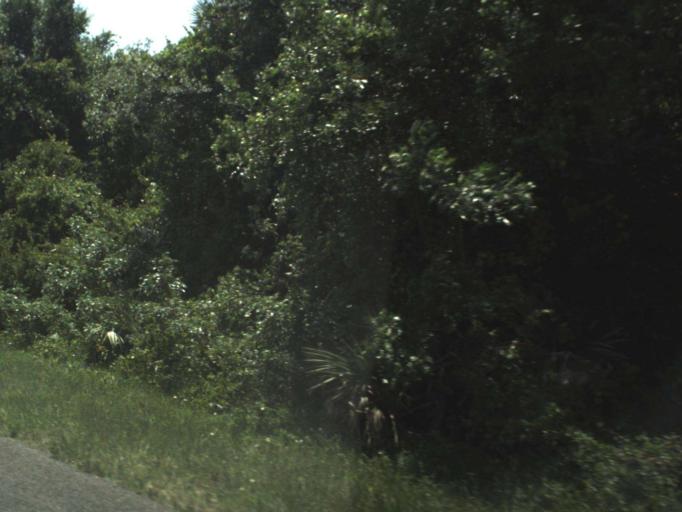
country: US
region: Florida
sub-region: Volusia County
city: Oak Hill
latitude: 28.7939
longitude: -80.8821
